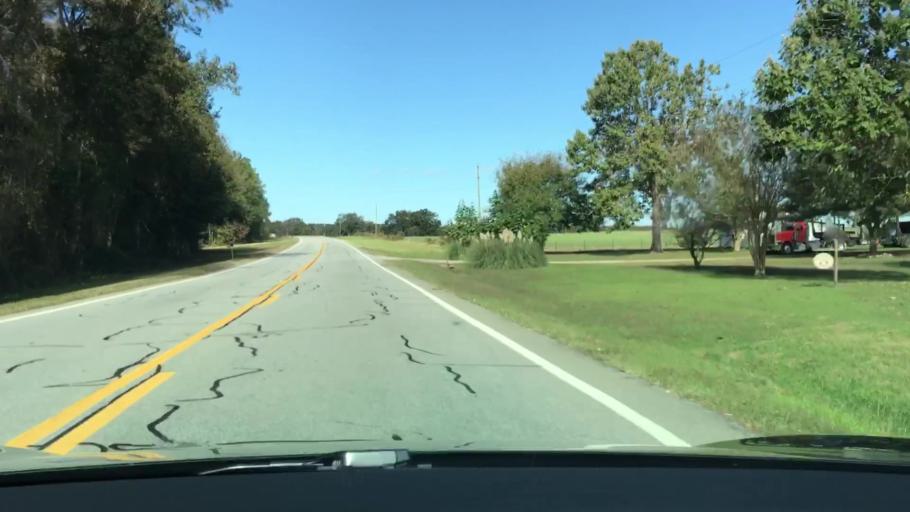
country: US
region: Georgia
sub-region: Glascock County
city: Gibson
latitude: 33.3402
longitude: -82.5734
